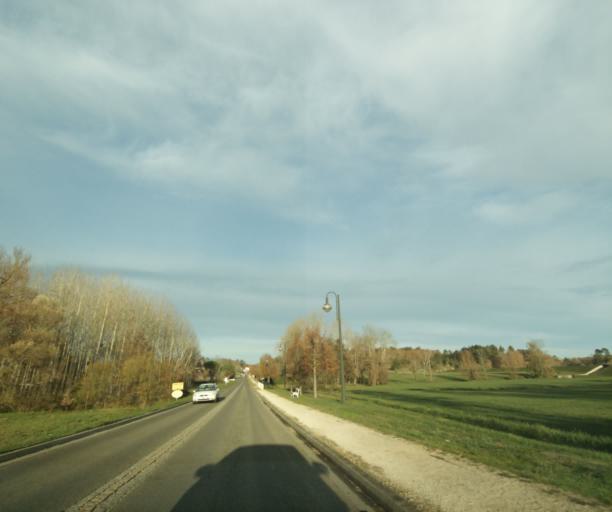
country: FR
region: Midi-Pyrenees
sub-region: Departement du Gers
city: Cazaubon
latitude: 43.9408
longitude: -0.0555
